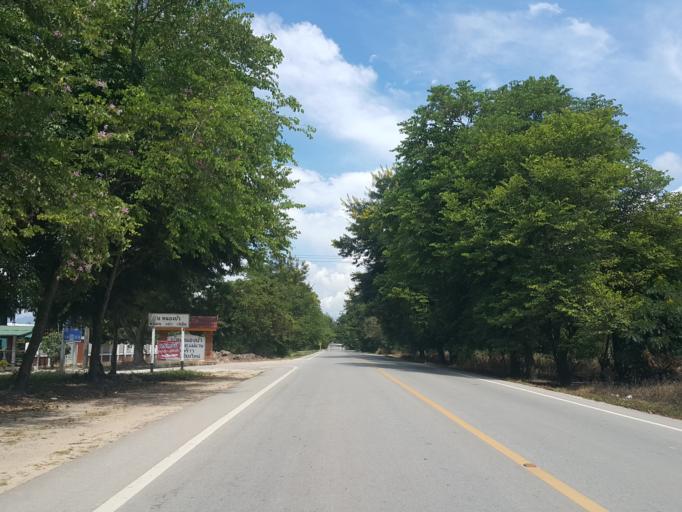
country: TH
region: Chiang Mai
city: Phrao
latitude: 19.2952
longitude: 99.1885
